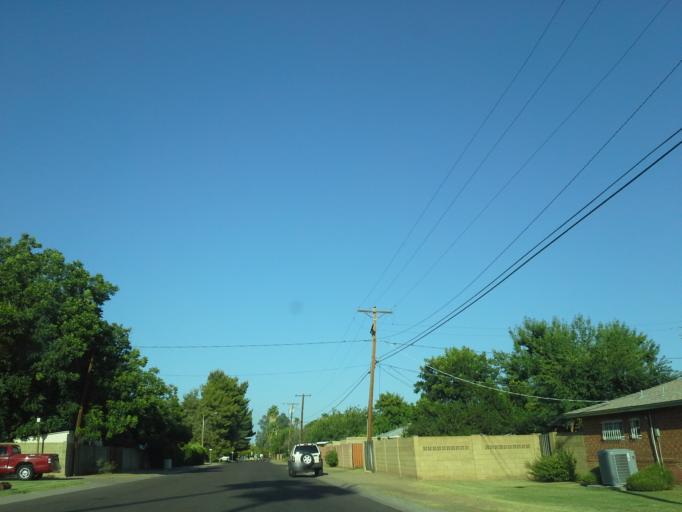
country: US
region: Arizona
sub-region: Maricopa County
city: Phoenix
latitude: 33.5277
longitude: -112.0944
